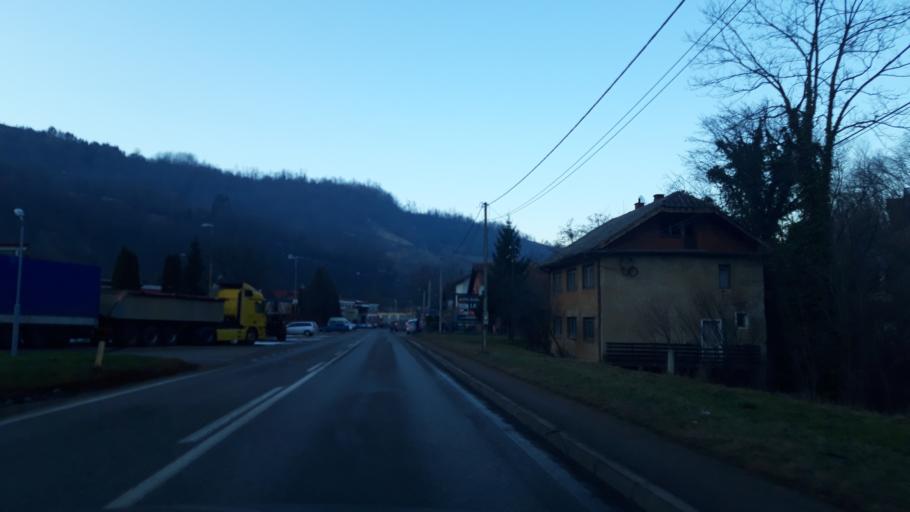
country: BA
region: Republika Srpska
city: Milici
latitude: 44.1745
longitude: 19.0757
